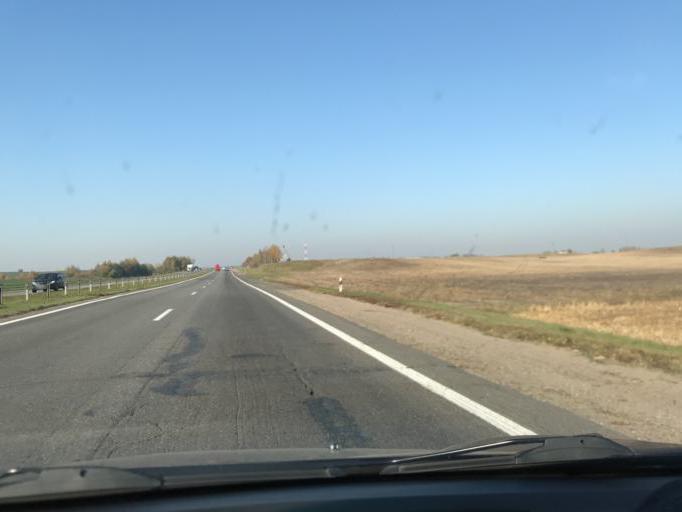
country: BY
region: Minsk
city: Luhavaya Slabada
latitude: 53.7256
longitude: 27.8581
